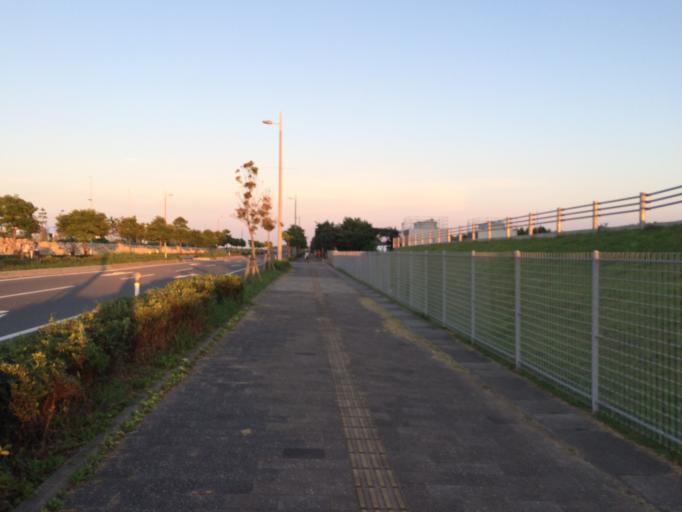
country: JP
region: Yamaguchi
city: Ogori-shimogo
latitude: 34.0092
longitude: 131.3733
